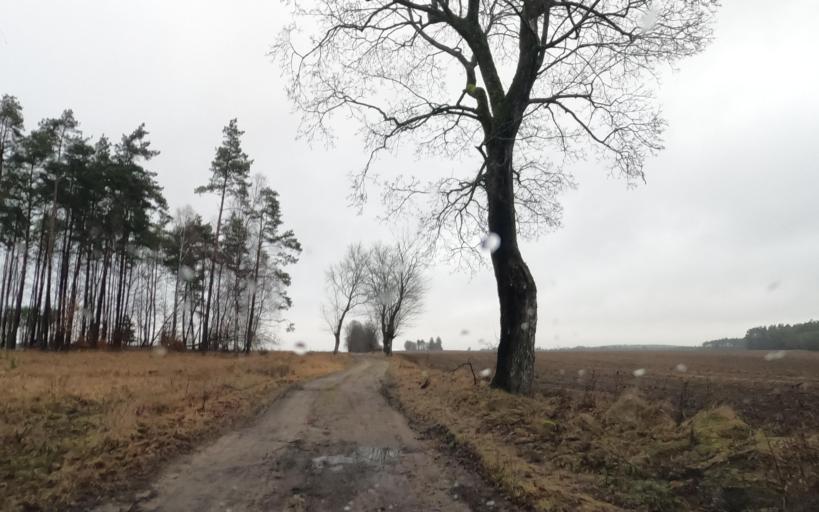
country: PL
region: West Pomeranian Voivodeship
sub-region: Powiat szczecinecki
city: Szczecinek
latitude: 53.6135
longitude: 16.6696
